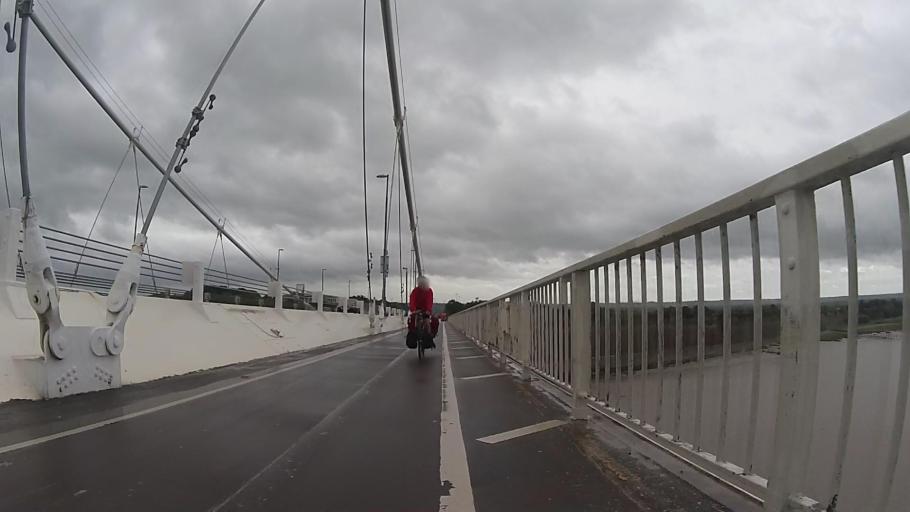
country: GB
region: England
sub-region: South Gloucestershire
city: Severn Beach
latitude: 51.6064
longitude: -2.6313
